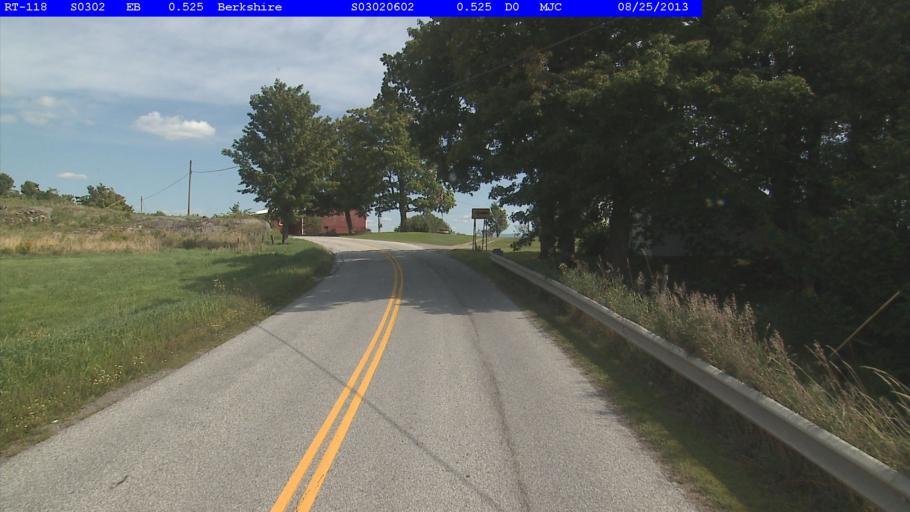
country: US
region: Vermont
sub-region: Franklin County
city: Enosburg Falls
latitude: 44.9842
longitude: -72.8052
